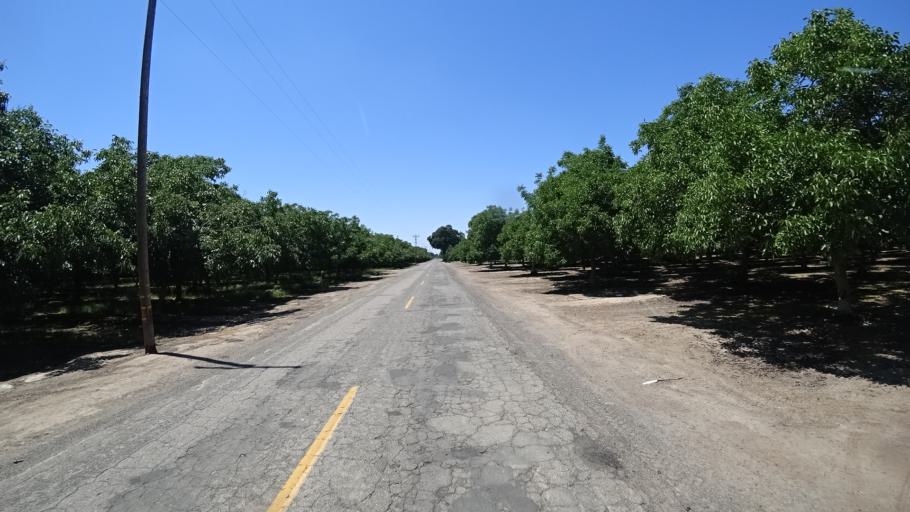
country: US
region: California
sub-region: Kings County
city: Lucerne
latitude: 36.4303
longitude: -119.5929
